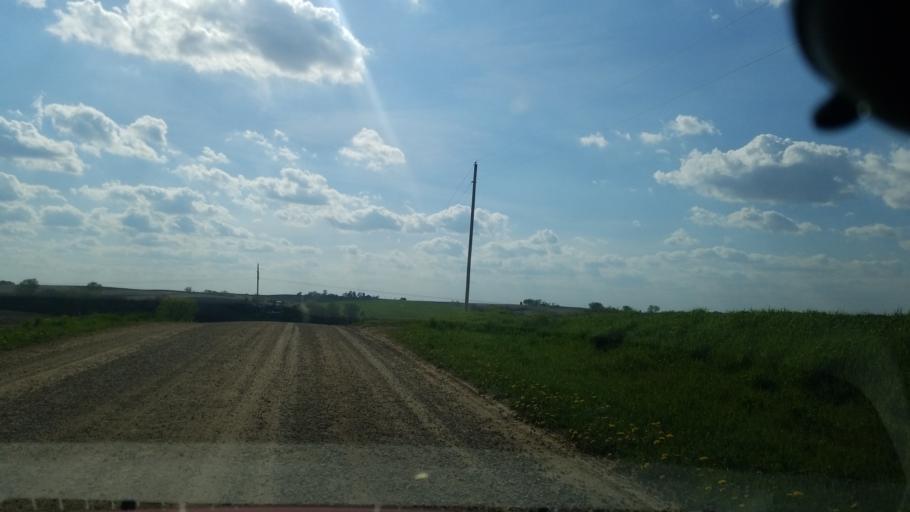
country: US
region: Iowa
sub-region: Jackson County
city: Maquoketa
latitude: 42.2149
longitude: -90.6871
